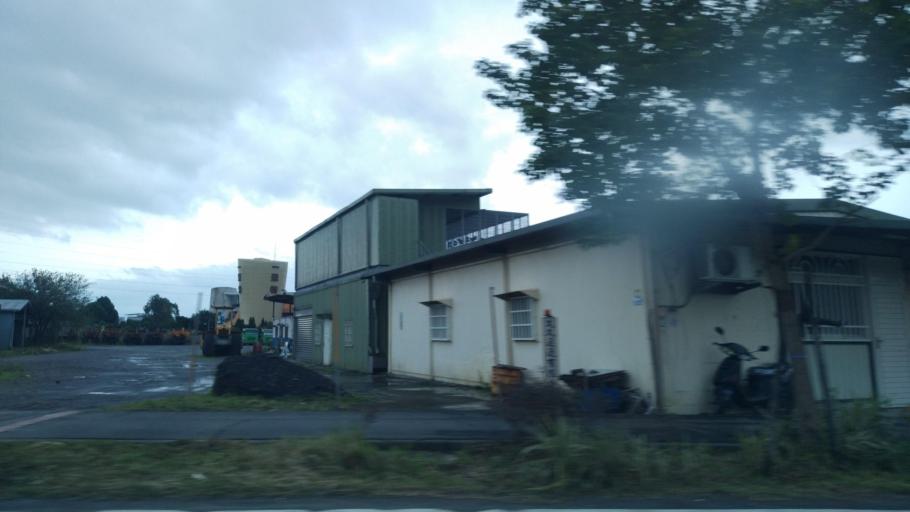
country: TW
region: Taiwan
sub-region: Yilan
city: Yilan
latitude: 24.6145
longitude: 121.8297
